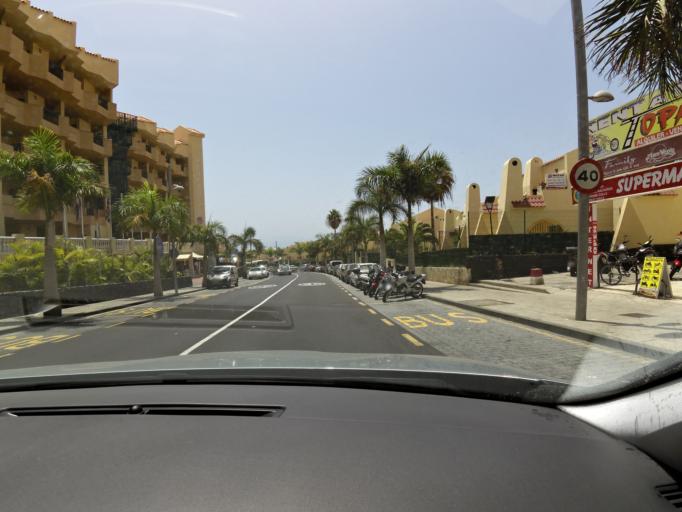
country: ES
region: Canary Islands
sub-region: Provincia de Santa Cruz de Tenerife
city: Playa de las Americas
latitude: 28.0863
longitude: -16.7300
